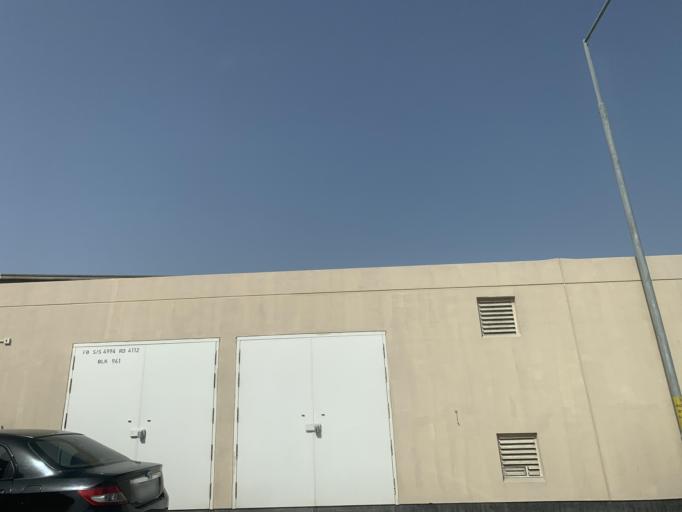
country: BH
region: Northern
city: Ar Rifa'
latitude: 26.1511
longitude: 50.5708
